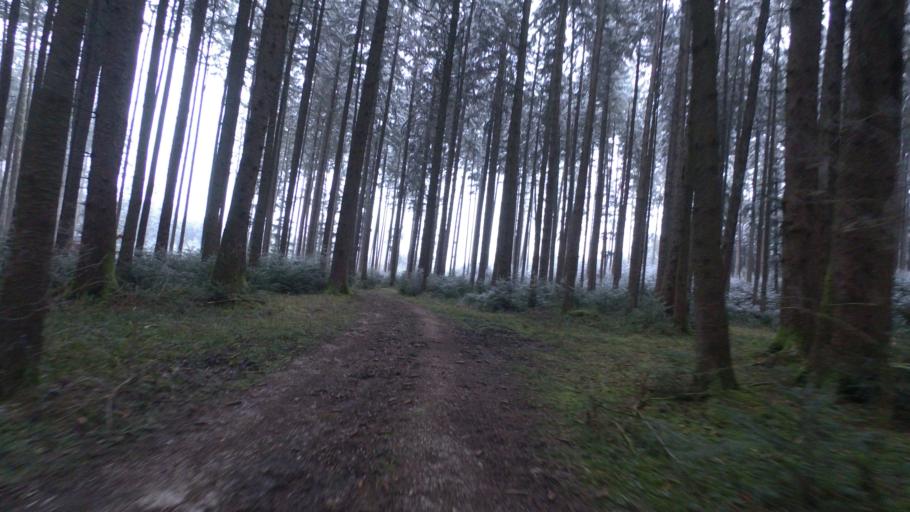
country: DE
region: Bavaria
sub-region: Upper Bavaria
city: Nussdorf
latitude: 47.8921
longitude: 12.5822
